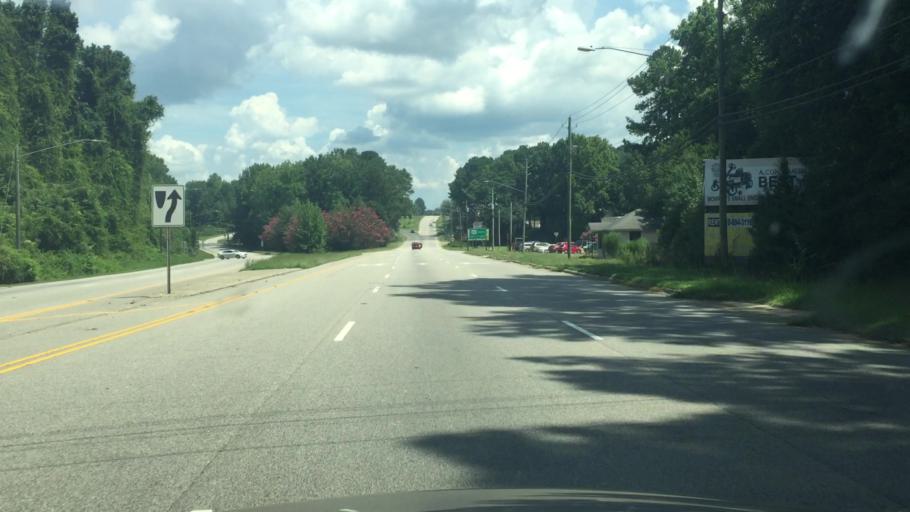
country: US
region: North Carolina
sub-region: Richmond County
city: Rockingham
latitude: 34.9219
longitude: -79.7823
